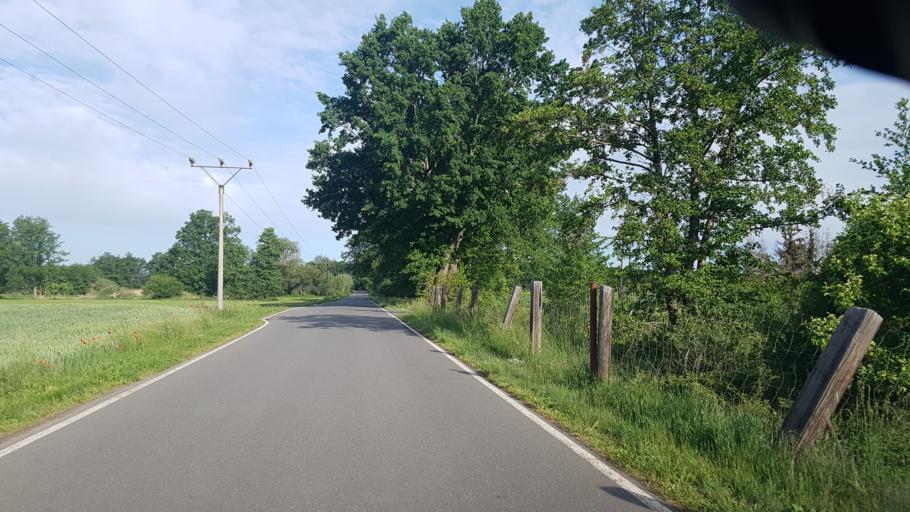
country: DE
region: Brandenburg
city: Luckau
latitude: 51.8261
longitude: 13.7552
